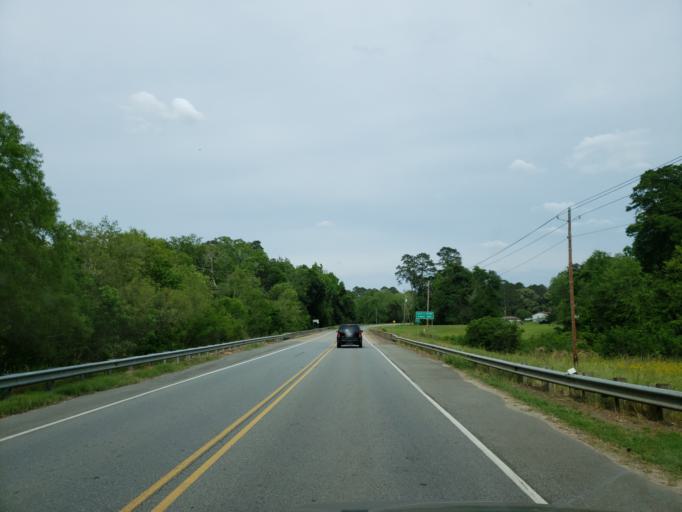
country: US
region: Georgia
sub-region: Dooly County
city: Vienna
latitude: 32.1113
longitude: -83.8372
